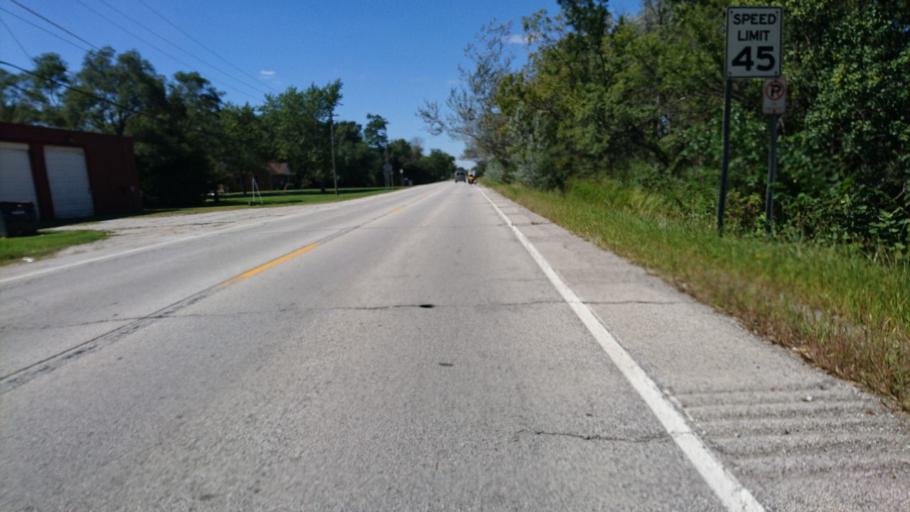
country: US
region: Illinois
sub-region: Cook County
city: Glenwood
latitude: 41.5427
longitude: -87.5862
